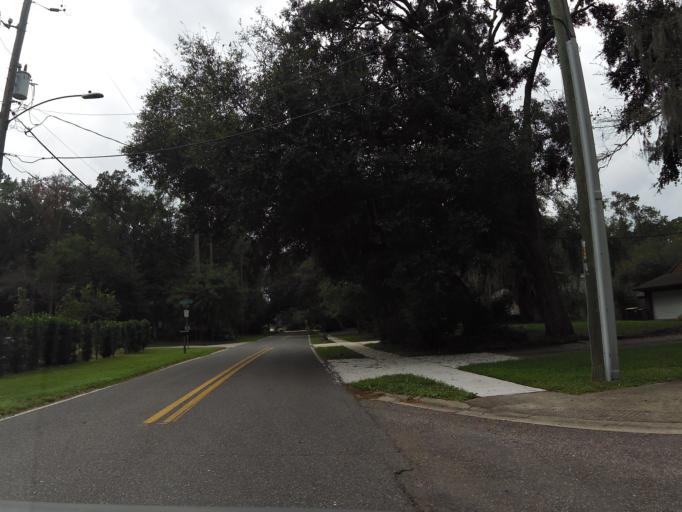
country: US
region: Florida
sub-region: Clay County
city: Bellair-Meadowbrook Terrace
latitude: 30.2572
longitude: -81.7206
